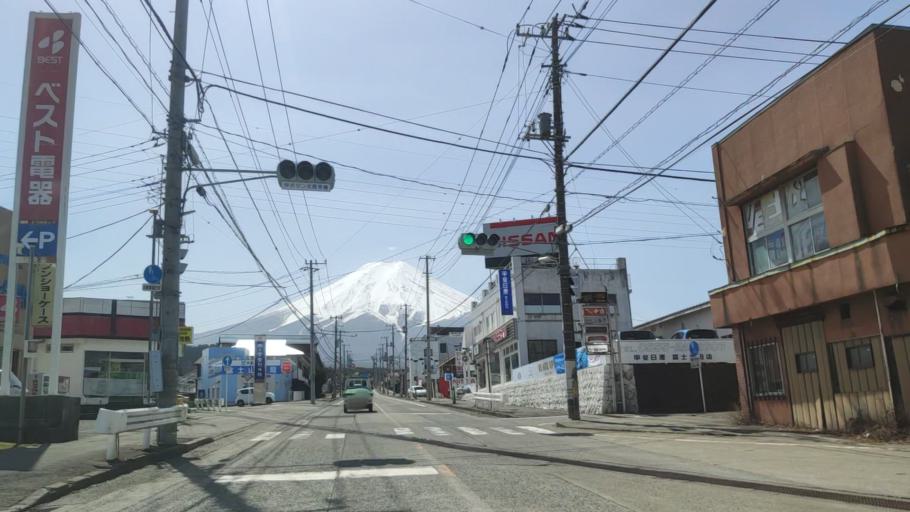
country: JP
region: Yamanashi
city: Fujikawaguchiko
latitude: 35.4743
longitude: 138.7995
